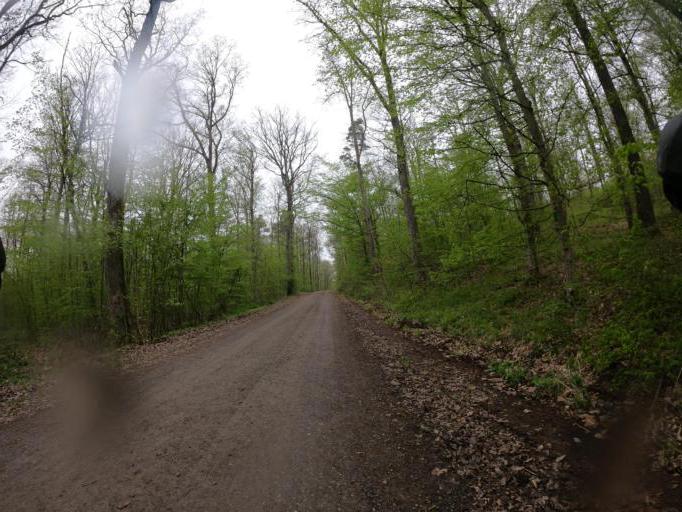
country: DE
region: Baden-Wuerttemberg
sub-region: Karlsruhe Region
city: Illingen
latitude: 48.9828
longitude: 8.8813
